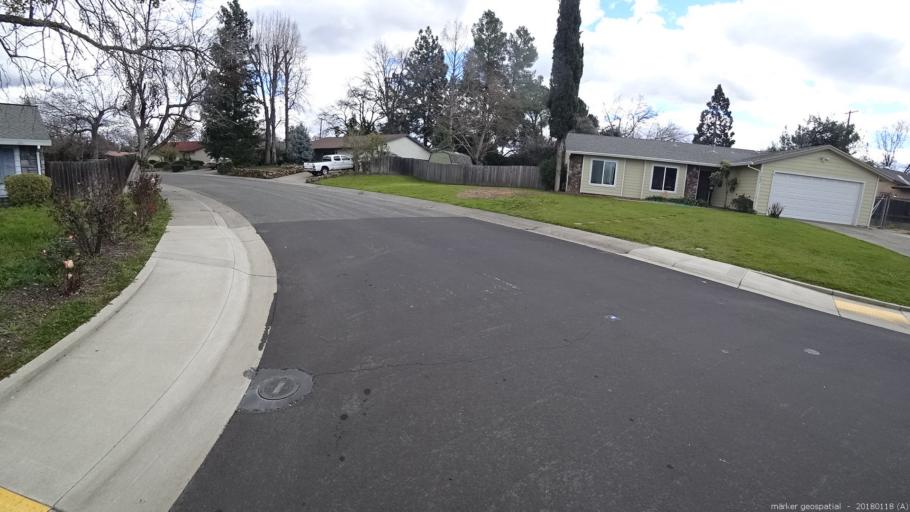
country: US
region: California
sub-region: Sacramento County
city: Orangevale
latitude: 38.6664
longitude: -121.2164
